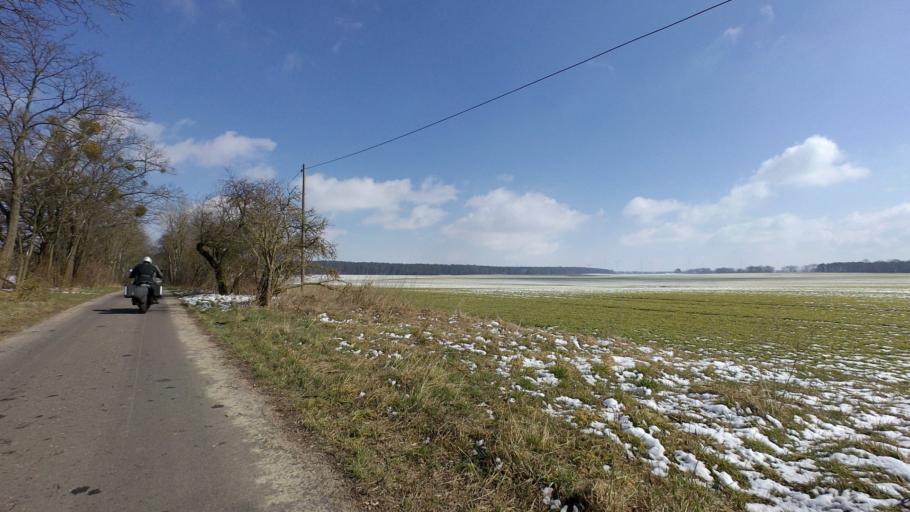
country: DE
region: Brandenburg
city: Werftpfuhl
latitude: 52.6994
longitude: 13.7808
